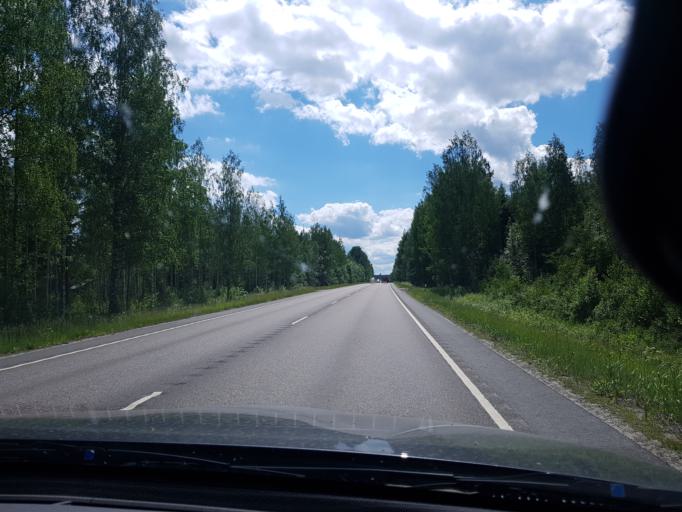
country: FI
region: Haeme
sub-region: Haemeenlinna
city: Parola
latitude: 61.1077
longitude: 24.4119
